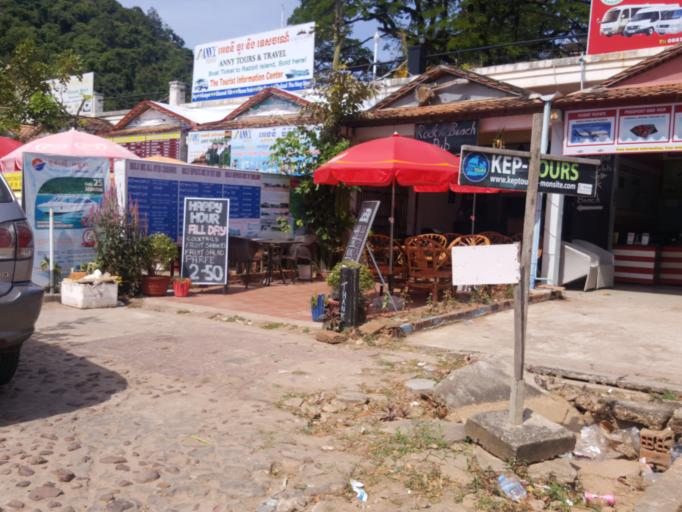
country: KH
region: Kep
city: Krong Kep
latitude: 10.4799
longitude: 104.2940
